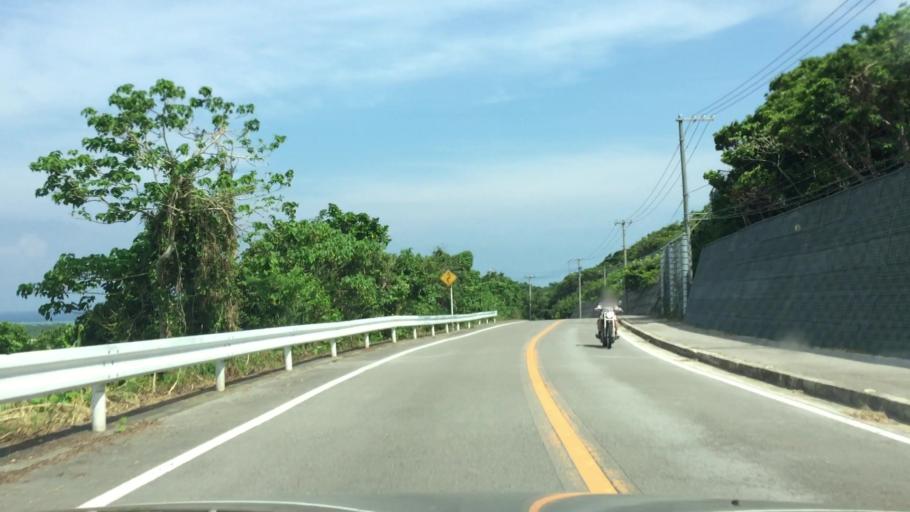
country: JP
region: Okinawa
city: Ishigaki
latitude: 24.5158
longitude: 124.2621
